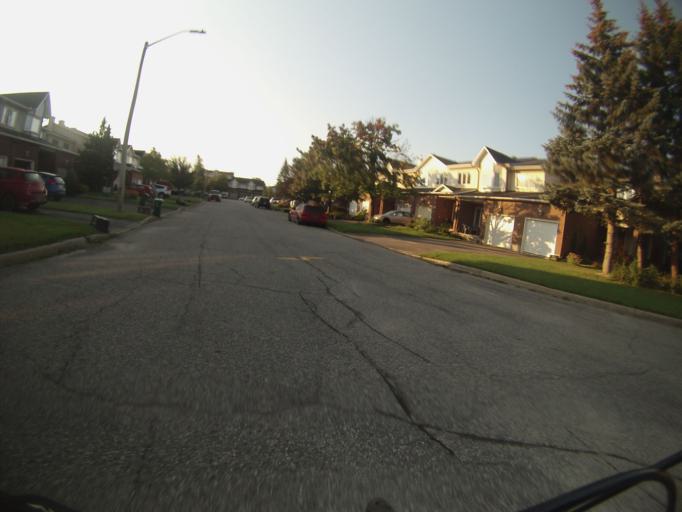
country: CA
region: Ontario
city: Ottawa
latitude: 45.3621
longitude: -75.6352
